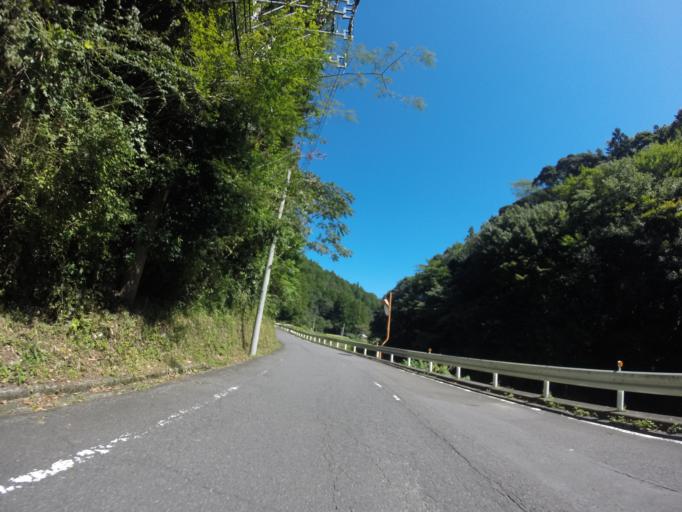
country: JP
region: Shizuoka
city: Kanaya
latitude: 34.9254
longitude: 138.1336
